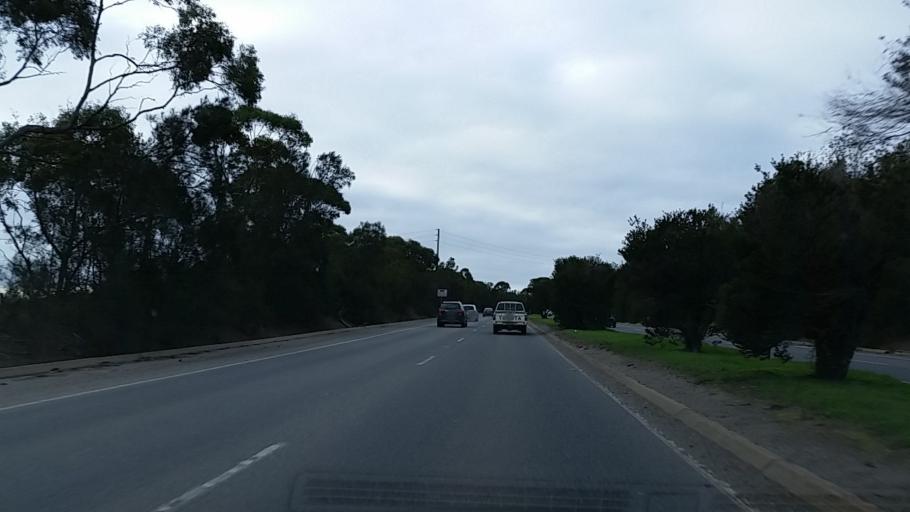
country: AU
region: South Australia
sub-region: Onkaparinga
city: Noarlunga
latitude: -35.1752
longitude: 138.4991
